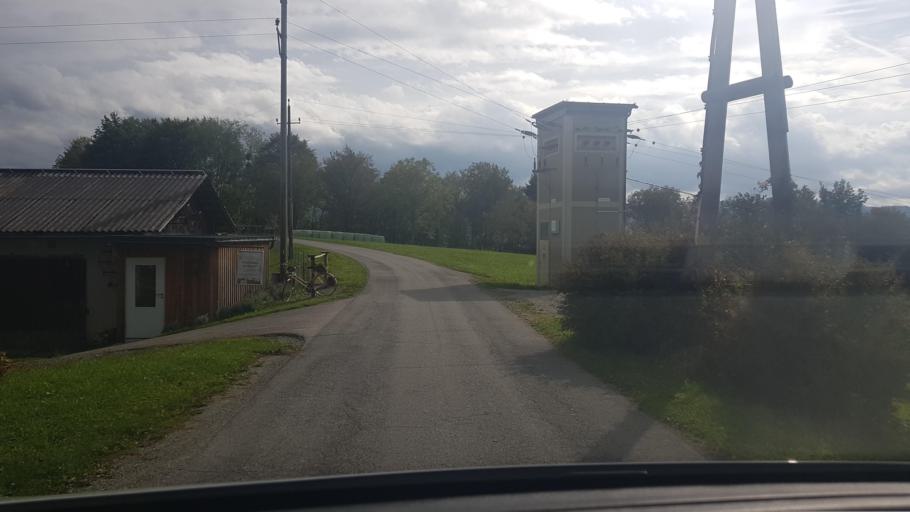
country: AT
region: Styria
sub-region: Politischer Bezirk Leibnitz
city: Sankt Johann im Saggautal
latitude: 46.6986
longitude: 15.4316
